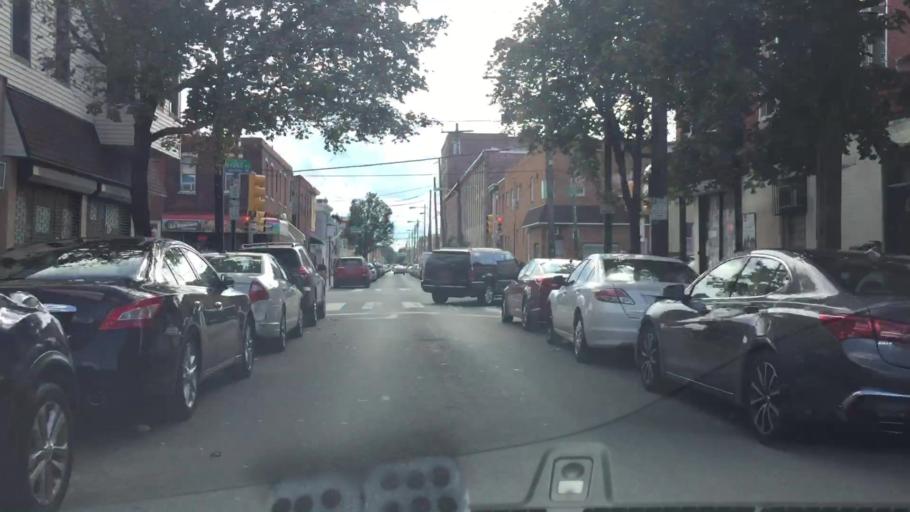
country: US
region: Pennsylvania
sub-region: Philadelphia County
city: Philadelphia
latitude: 39.9243
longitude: -75.1660
